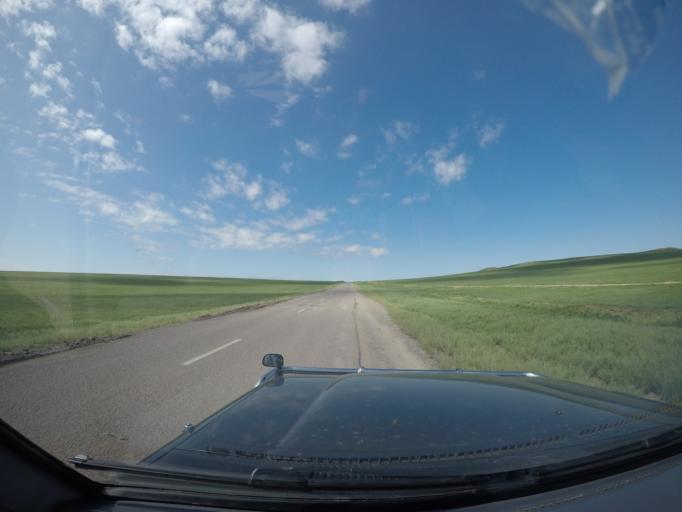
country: MN
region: Suhbaatar
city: Hanhohiy
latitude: 47.3810
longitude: 111.8185
